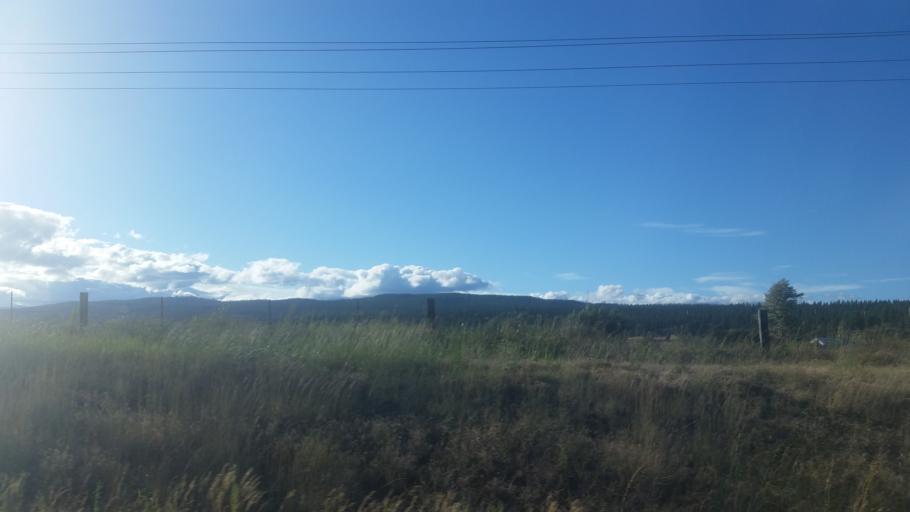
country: US
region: Washington
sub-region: Kittitas County
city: Cle Elum
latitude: 47.1813
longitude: -120.8351
